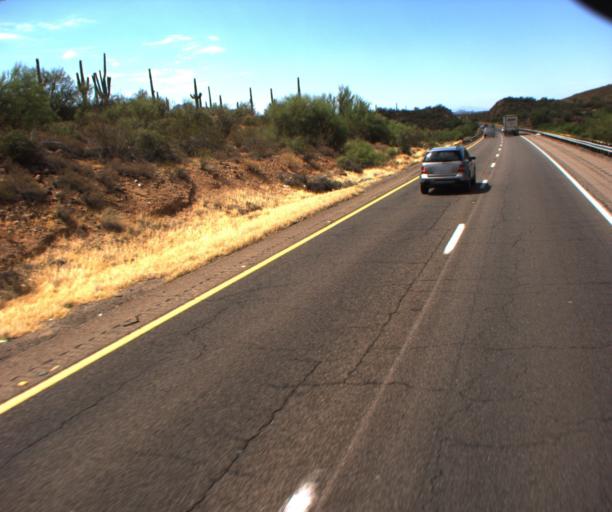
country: US
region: Arizona
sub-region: Maricopa County
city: New River
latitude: 33.9510
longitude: -112.1393
